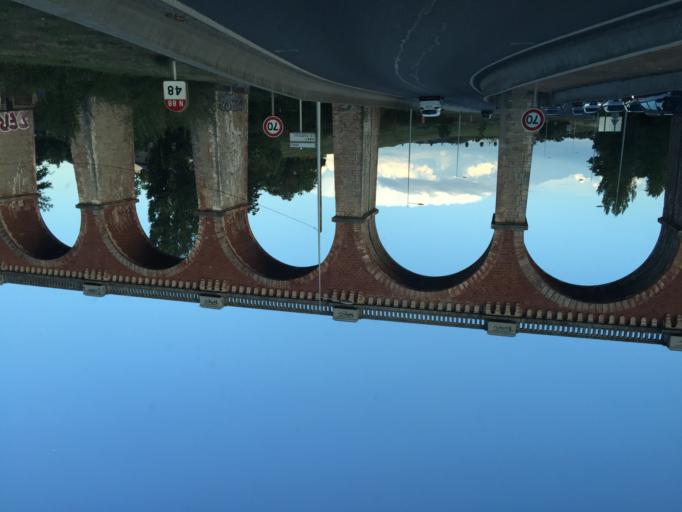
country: FR
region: Midi-Pyrenees
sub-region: Departement de l'Aveyron
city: Rodez
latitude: 44.3637
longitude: 2.5759
